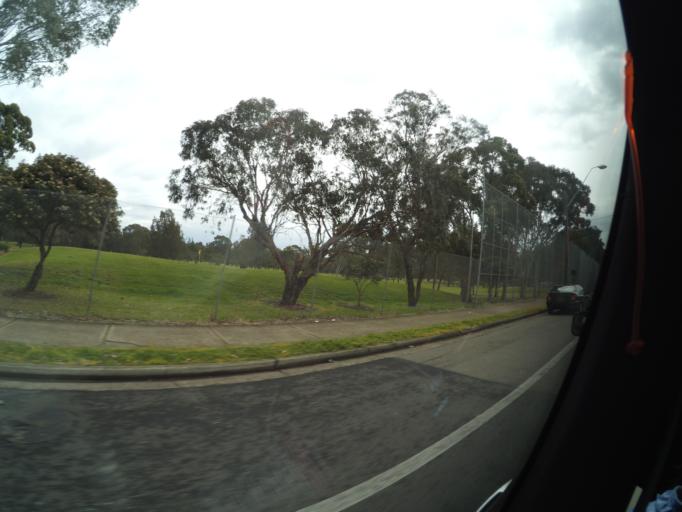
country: AU
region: New South Wales
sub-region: Bankstown
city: Regents Park
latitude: -33.8674
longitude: 151.0179
